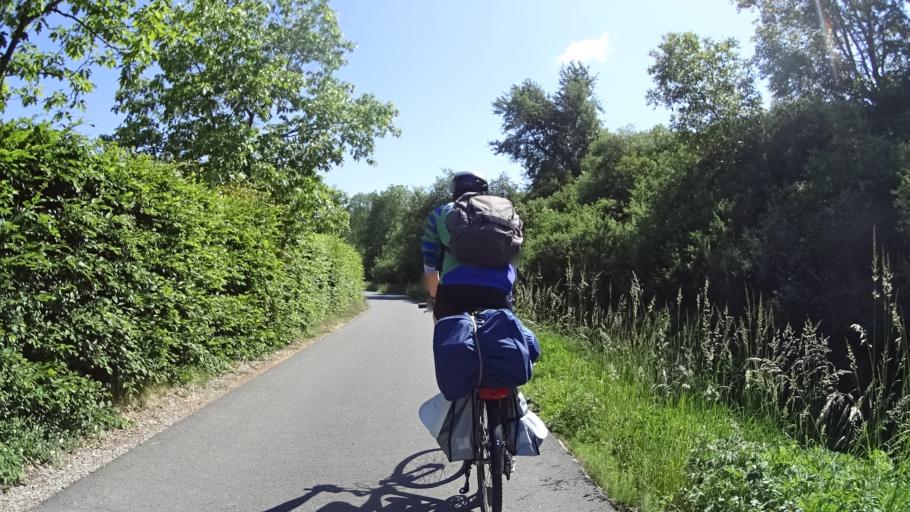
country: DE
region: Baden-Wuerttemberg
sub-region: Regierungsbezirk Stuttgart
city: Weikersheim
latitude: 49.4717
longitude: 9.8935
